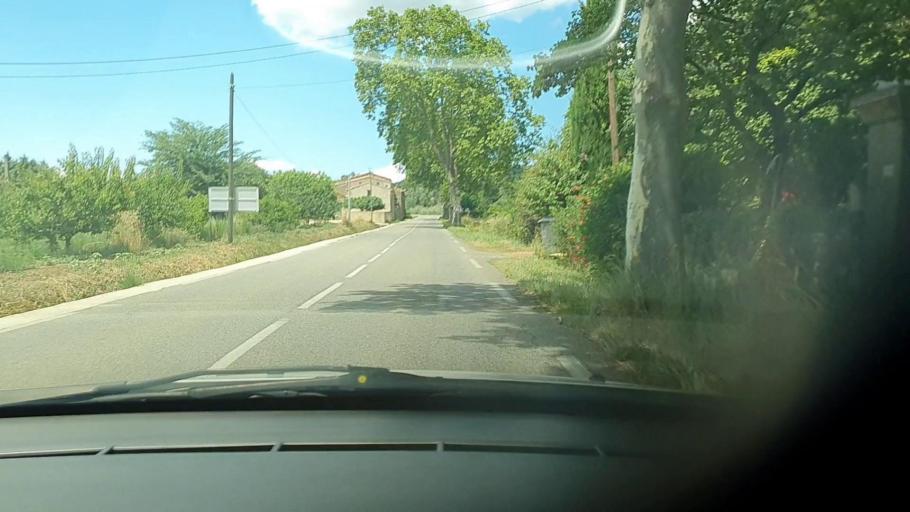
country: FR
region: Languedoc-Roussillon
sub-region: Departement du Gard
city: Saint-Chaptes
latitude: 44.0528
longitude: 4.2869
